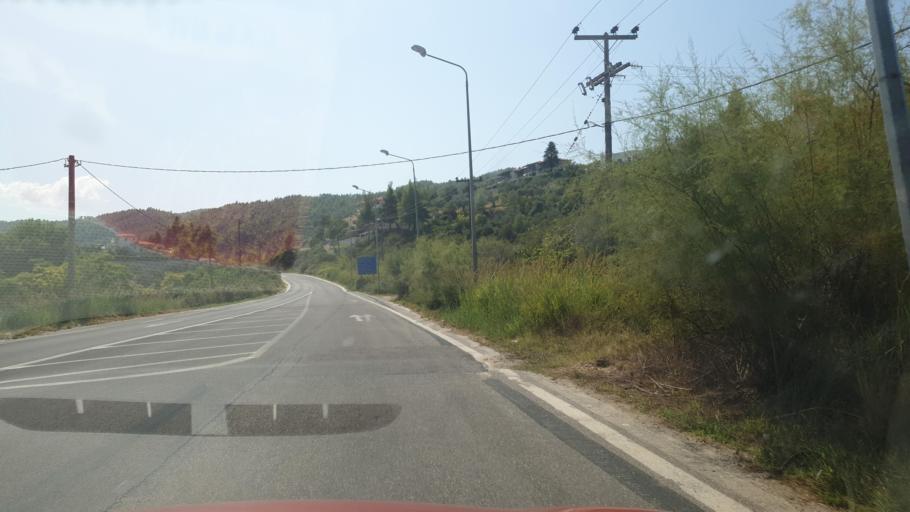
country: GR
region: Central Macedonia
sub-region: Nomos Chalkidikis
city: Agios Nikolaos
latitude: 40.1913
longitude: 23.7703
